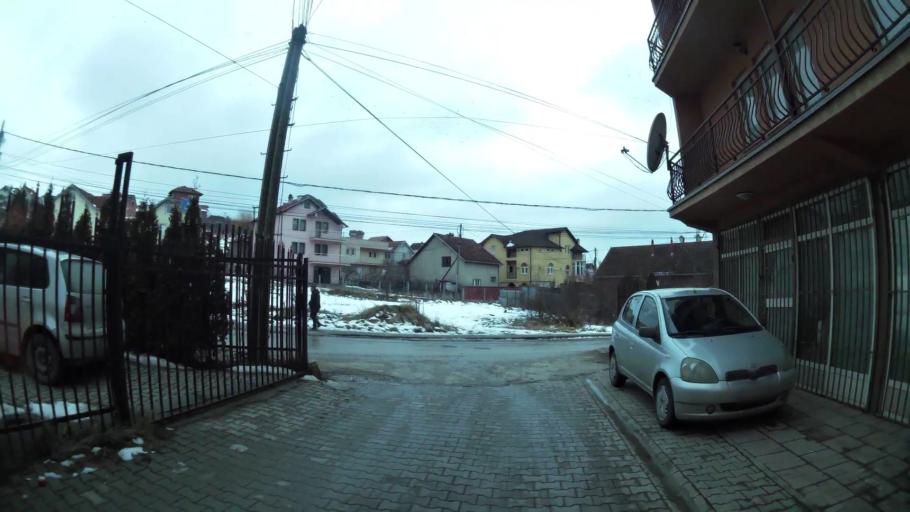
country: XK
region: Pristina
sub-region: Komuna e Prishtines
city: Pristina
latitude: 42.6420
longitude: 21.1703
